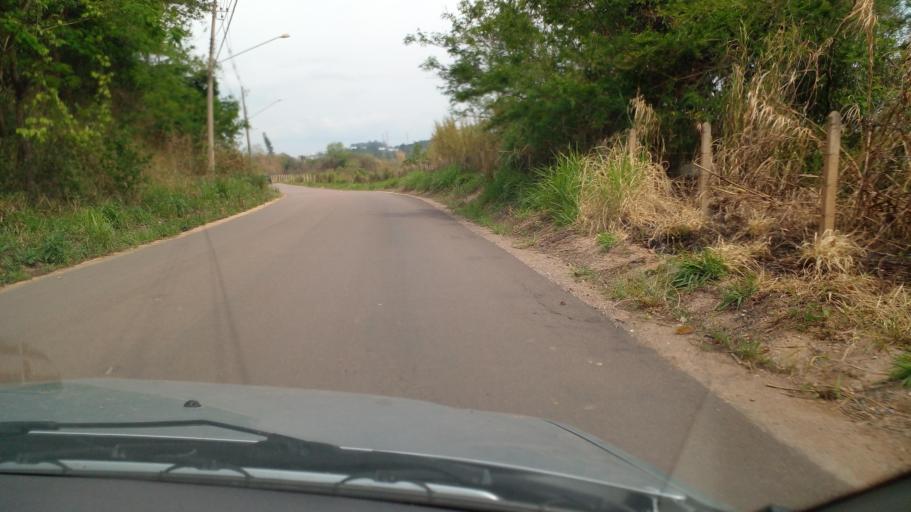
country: BR
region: Sao Paulo
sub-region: Jundiai
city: Jundiai
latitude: -23.1443
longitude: -46.8817
